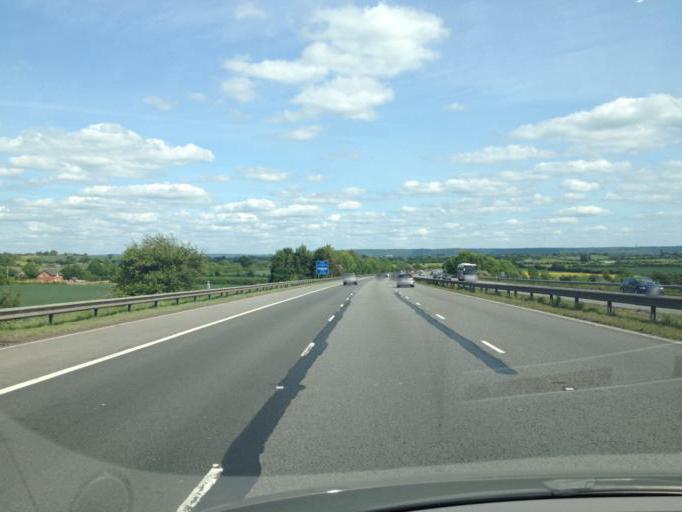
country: GB
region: England
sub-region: Oxfordshire
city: Chalgrove
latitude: 51.7212
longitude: -1.0409
